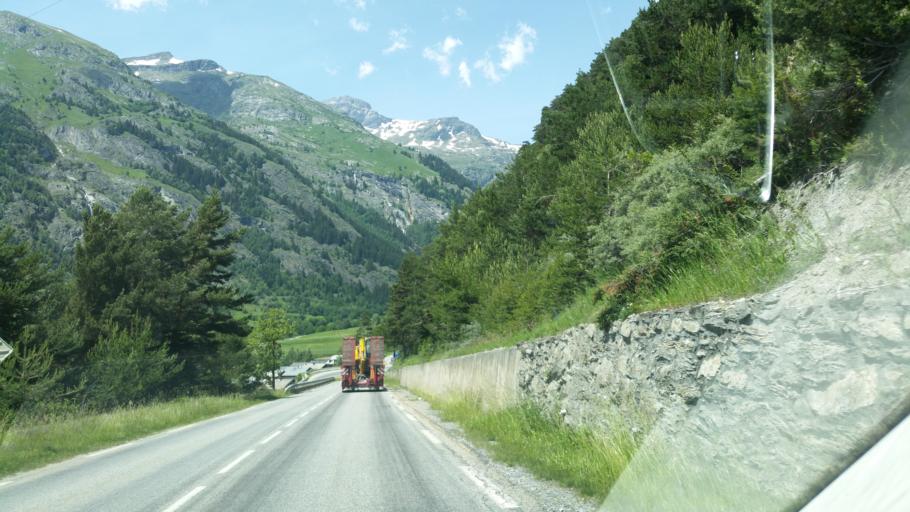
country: FR
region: Rhone-Alpes
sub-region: Departement de la Savoie
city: Modane
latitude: 45.2796
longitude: 6.8174
